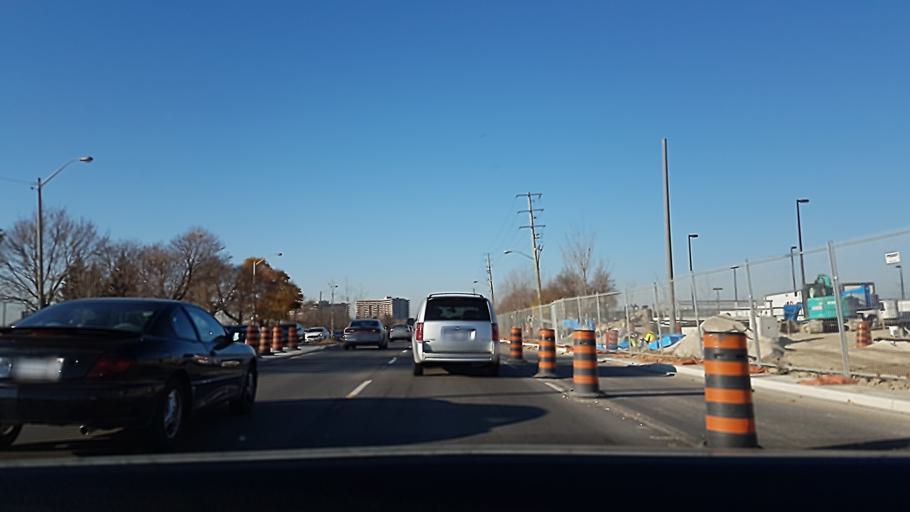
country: CA
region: Ontario
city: Concord
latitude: 43.7777
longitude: -79.5117
